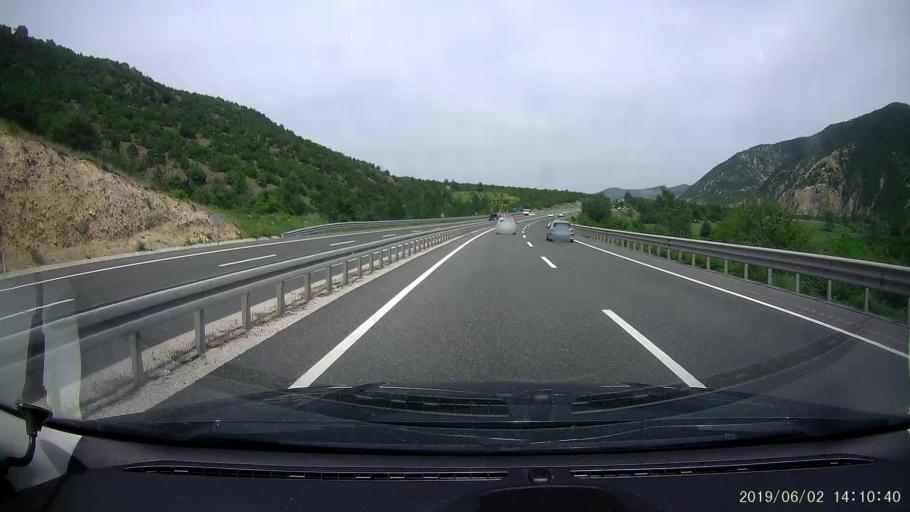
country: TR
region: Cankiri
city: Ilgaz
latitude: 40.9040
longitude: 33.7701
